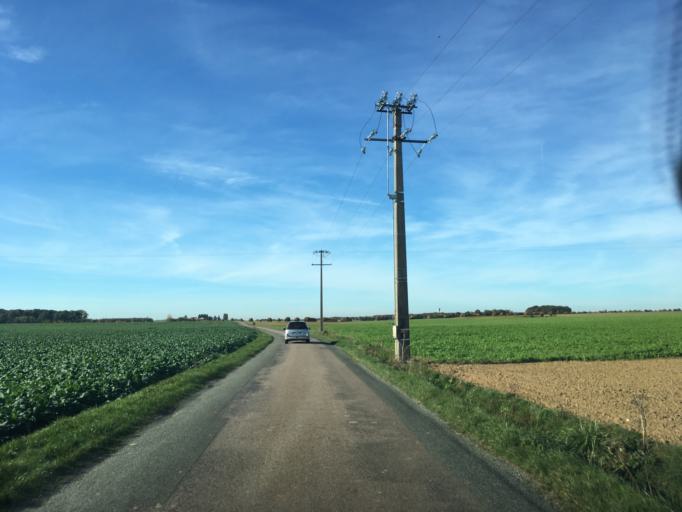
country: FR
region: Haute-Normandie
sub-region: Departement de l'Eure
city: Pacy-sur-Eure
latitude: 49.0404
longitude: 1.4199
